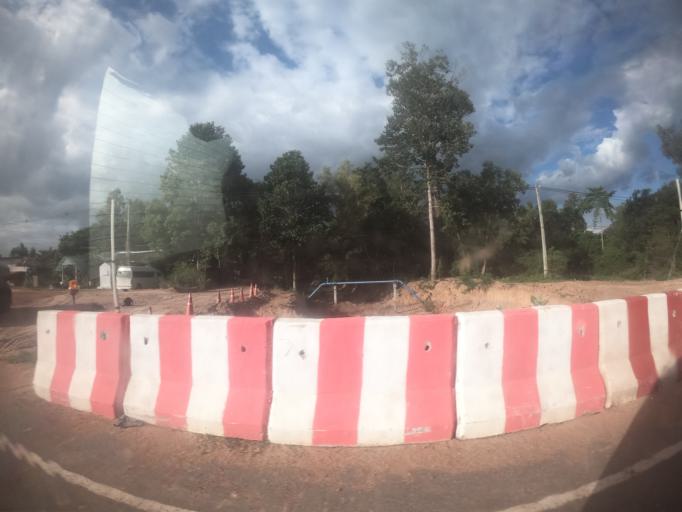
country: TH
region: Surin
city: Kap Choeng
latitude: 14.4791
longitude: 103.5866
